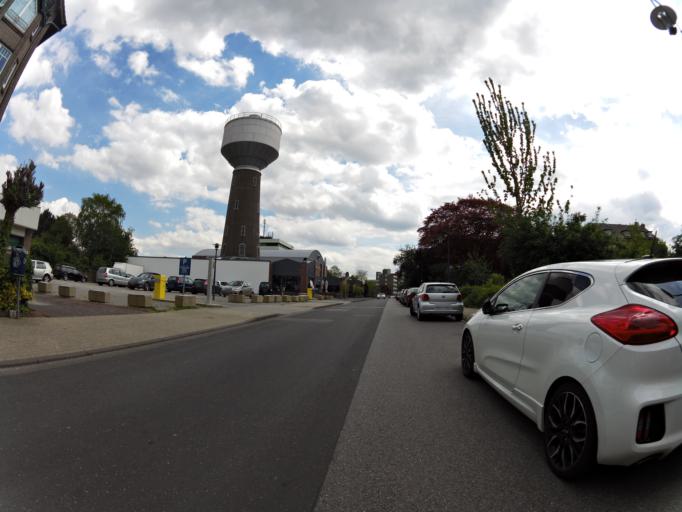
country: DE
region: North Rhine-Westphalia
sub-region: Regierungsbezirk Koln
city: Alsdorf
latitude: 50.8759
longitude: 6.1644
